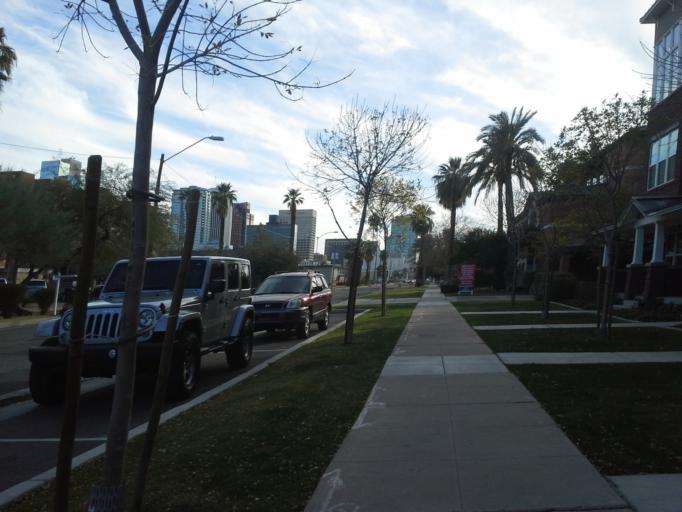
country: US
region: Arizona
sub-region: Maricopa County
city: Phoenix
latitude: 33.4575
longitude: -112.0778
